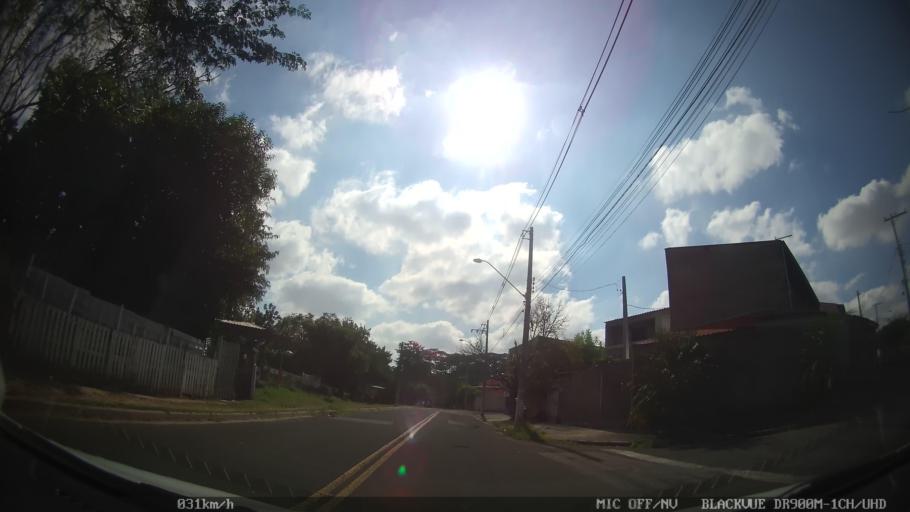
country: BR
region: Sao Paulo
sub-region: Campinas
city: Campinas
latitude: -22.9382
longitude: -47.1226
